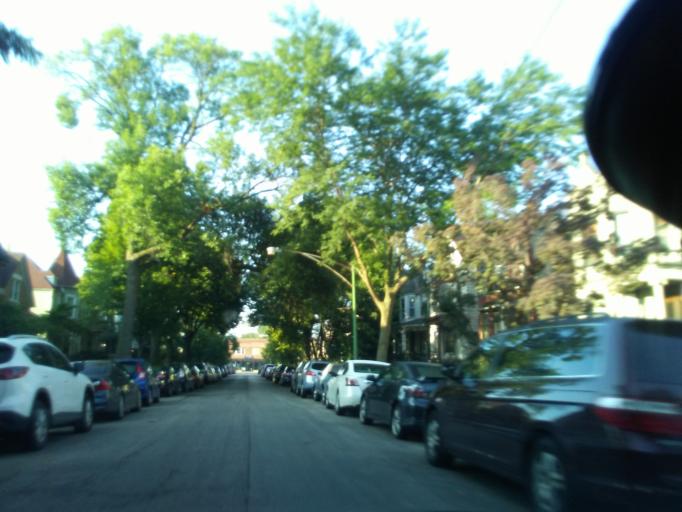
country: US
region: Illinois
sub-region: Cook County
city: Lincolnwood
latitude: 41.9261
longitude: -87.7158
